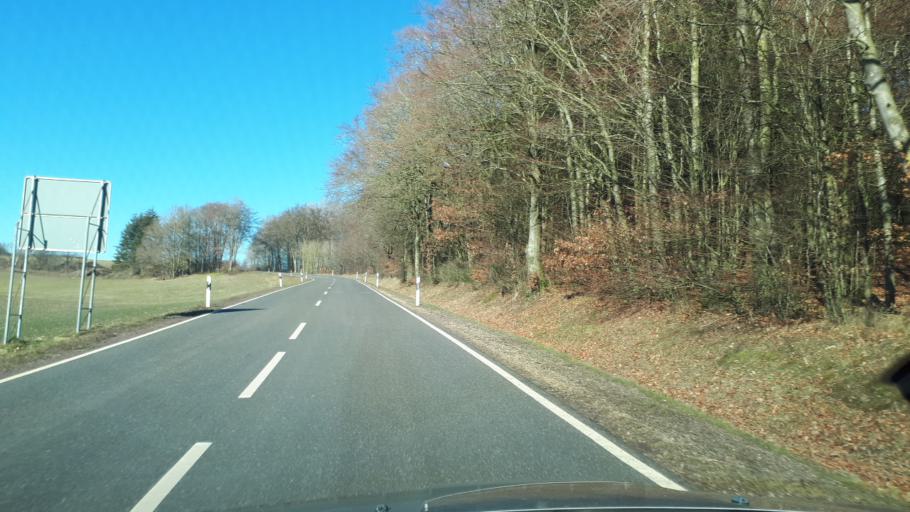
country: DE
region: Rheinland-Pfalz
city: Ellscheid
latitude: 50.1441
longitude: 6.9310
